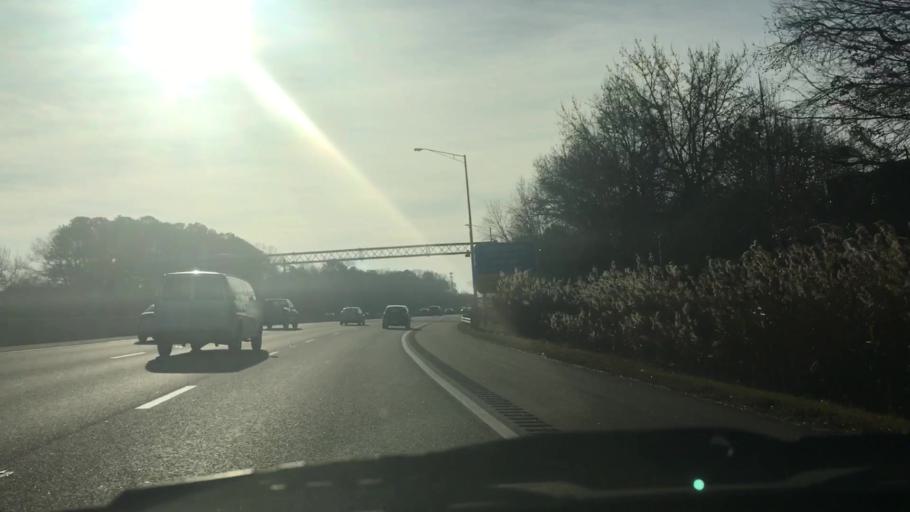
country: US
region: Virginia
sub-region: City of Norfolk
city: Norfolk
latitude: 36.9007
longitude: -76.2357
